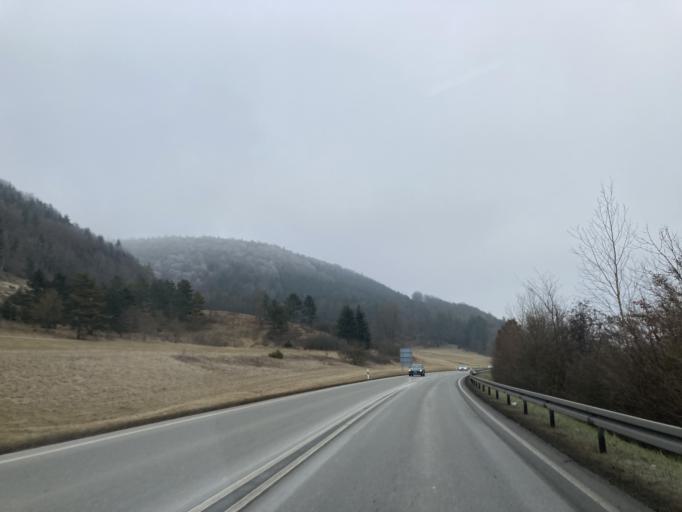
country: DE
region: Baden-Wuerttemberg
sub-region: Freiburg Region
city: Geisingen
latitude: 47.9263
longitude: 8.6790
